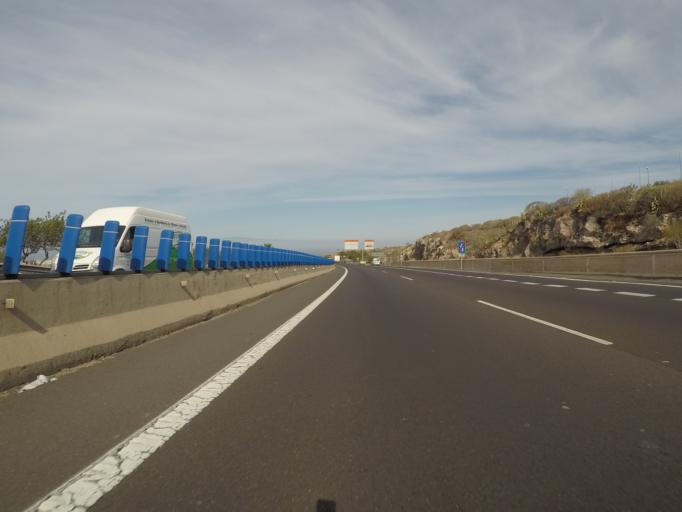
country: ES
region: Canary Islands
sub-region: Provincia de Santa Cruz de Tenerife
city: Playa de las Americas
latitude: 28.0638
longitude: -16.7085
